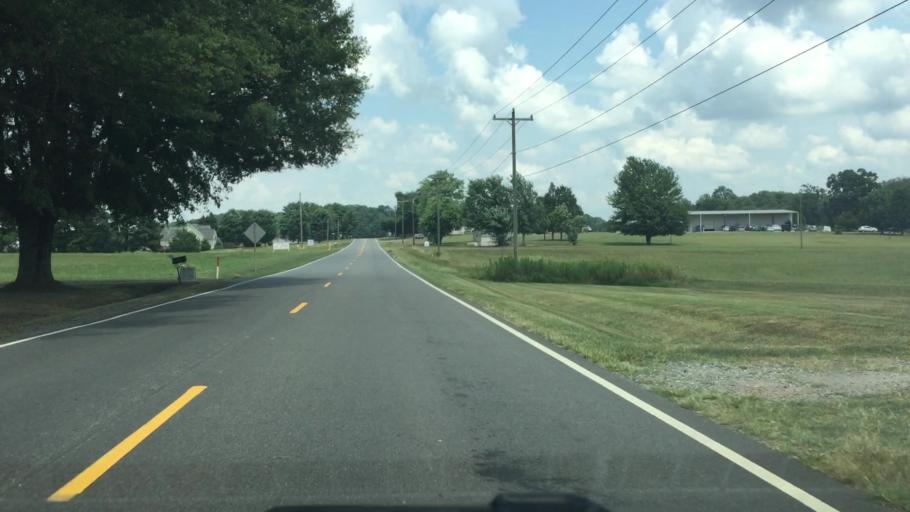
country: US
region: North Carolina
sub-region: Iredell County
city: Troutman
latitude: 35.7180
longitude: -80.8835
